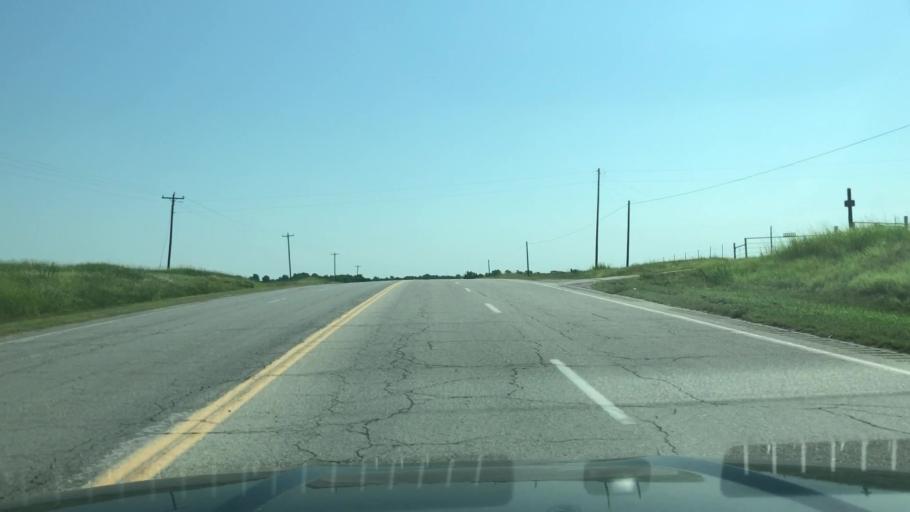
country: US
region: Oklahoma
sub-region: Creek County
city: Drumright
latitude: 35.9931
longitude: -96.5348
